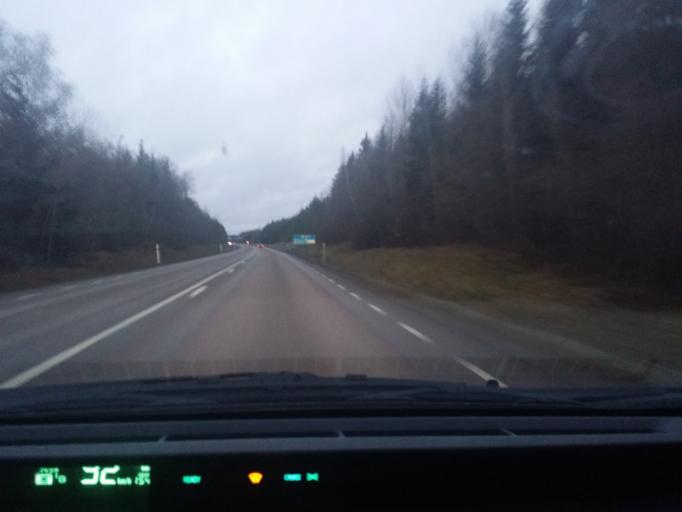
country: SE
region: Soedermanland
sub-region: Eskilstuna Kommun
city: Kvicksund
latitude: 59.4886
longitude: 16.3056
